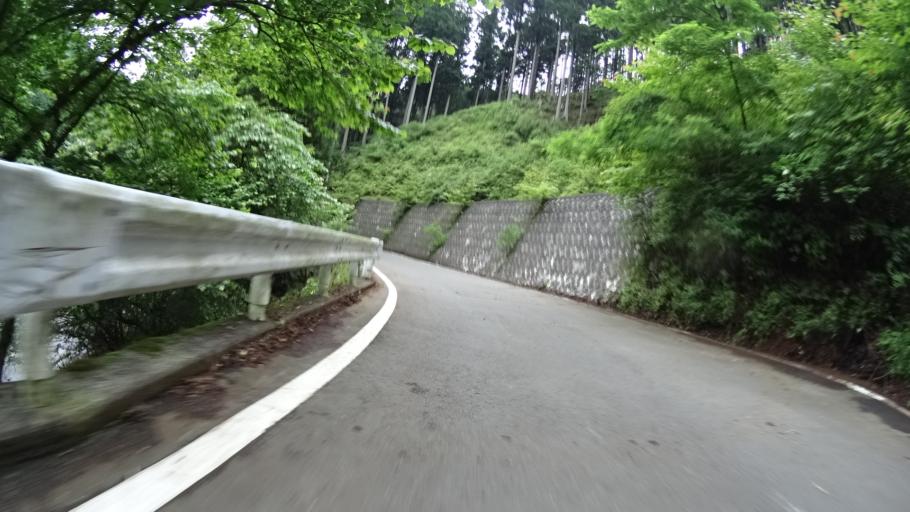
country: JP
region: Kanagawa
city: Hadano
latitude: 35.4549
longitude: 139.2136
